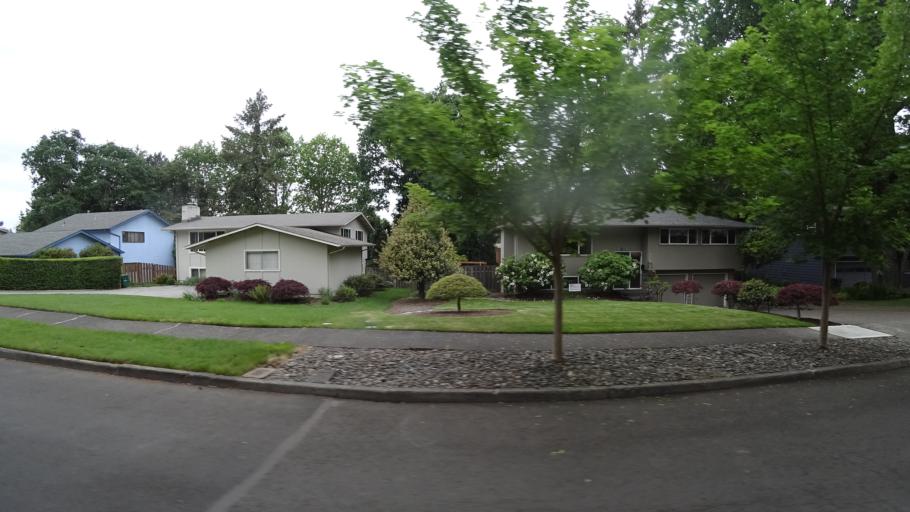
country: US
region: Oregon
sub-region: Washington County
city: Raleigh Hills
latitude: 45.4767
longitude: -122.7748
